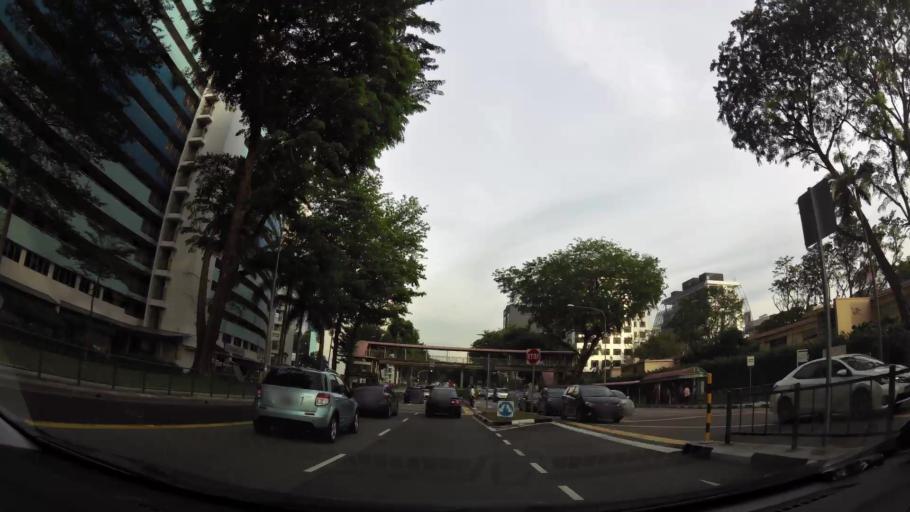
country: SG
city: Singapore
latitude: 1.2864
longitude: 103.8067
